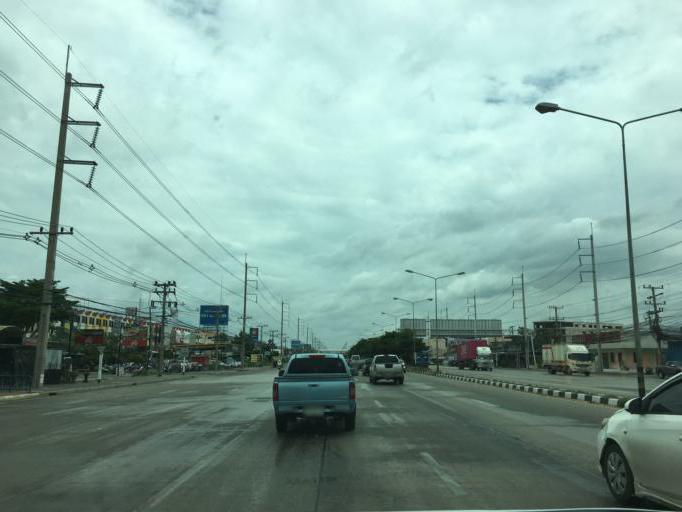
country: TH
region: Phra Nakhon Si Ayutthaya
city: Uthai
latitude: 14.3113
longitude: 100.6425
